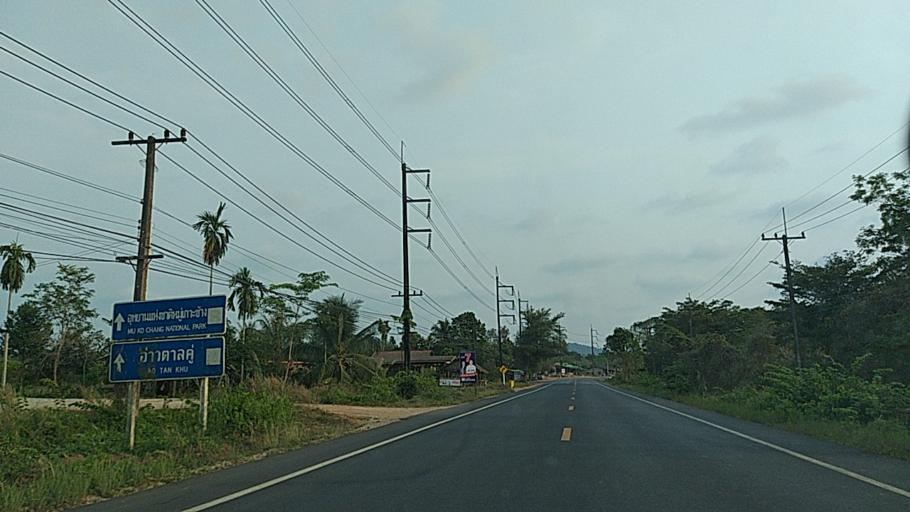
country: TH
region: Trat
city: Khao Saming
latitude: 12.3326
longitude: 102.3703
